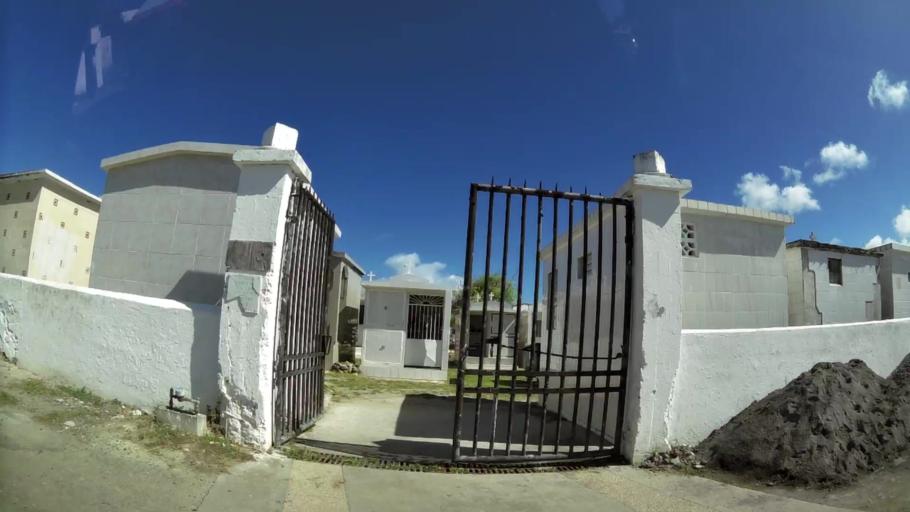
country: GP
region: Guadeloupe
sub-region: Guadeloupe
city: Le Moule
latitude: 16.3304
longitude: -61.3479
